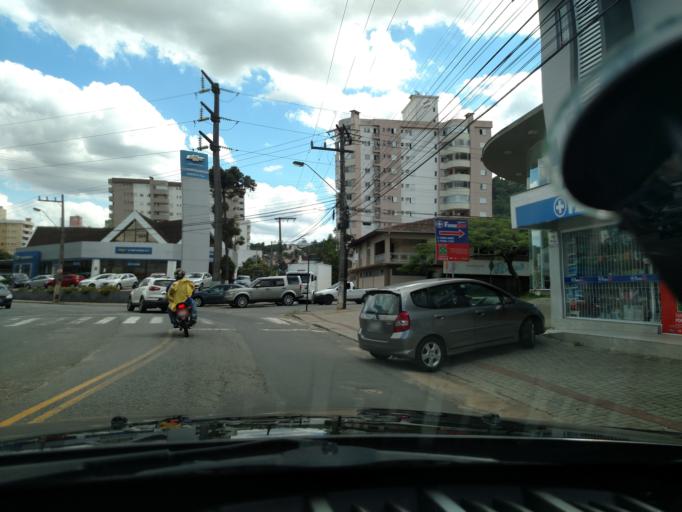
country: BR
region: Santa Catarina
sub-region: Blumenau
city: Blumenau
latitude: -26.8960
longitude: -49.0866
